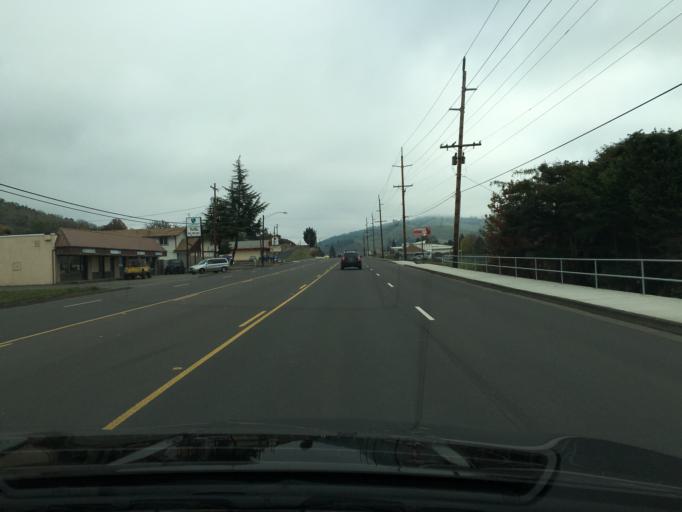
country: US
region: Oregon
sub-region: Douglas County
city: Roseburg
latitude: 43.2130
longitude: -123.3177
